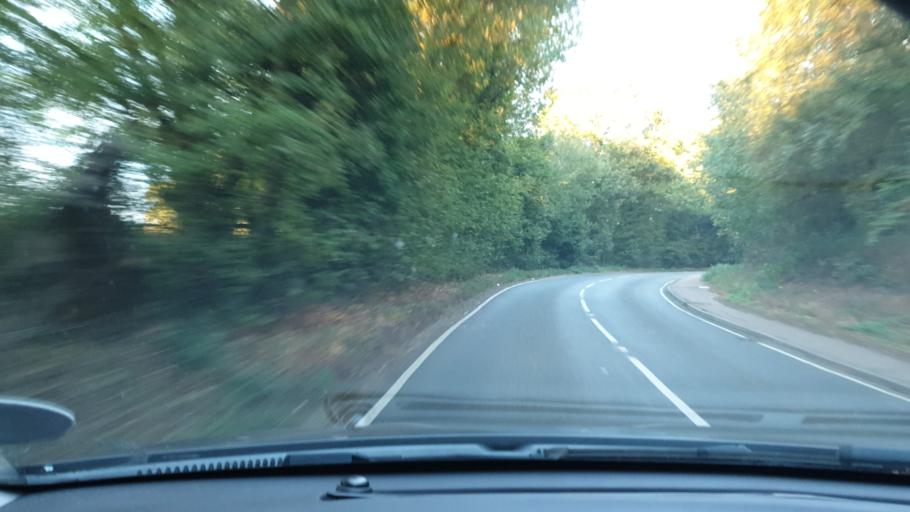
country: GB
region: England
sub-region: Essex
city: Rowhedge
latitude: 51.8976
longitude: 0.9511
